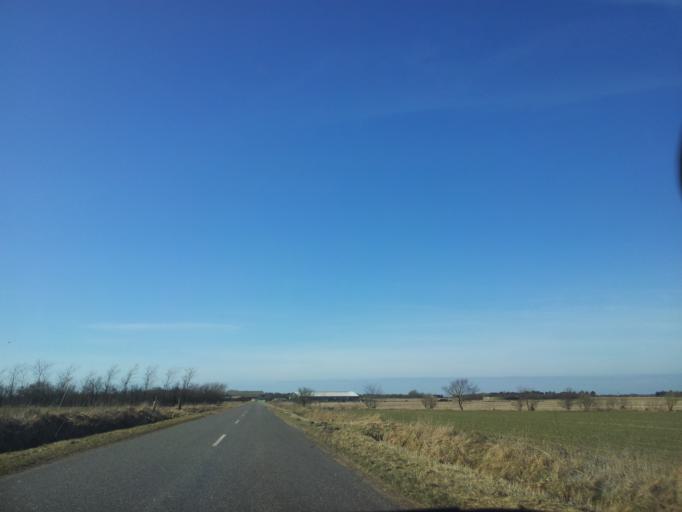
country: DK
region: South Denmark
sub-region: Tonder Kommune
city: Sherrebek
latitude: 55.1715
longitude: 8.7326
